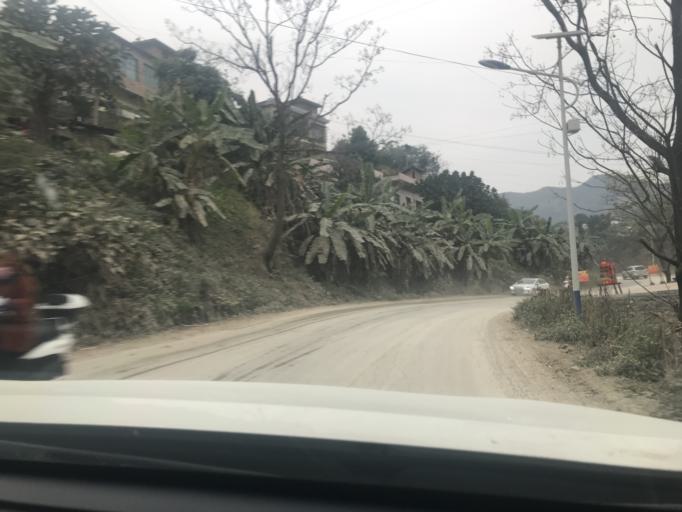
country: CN
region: Guangxi Zhuangzu Zizhiqu
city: Xinzhou
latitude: 24.9850
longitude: 105.8205
